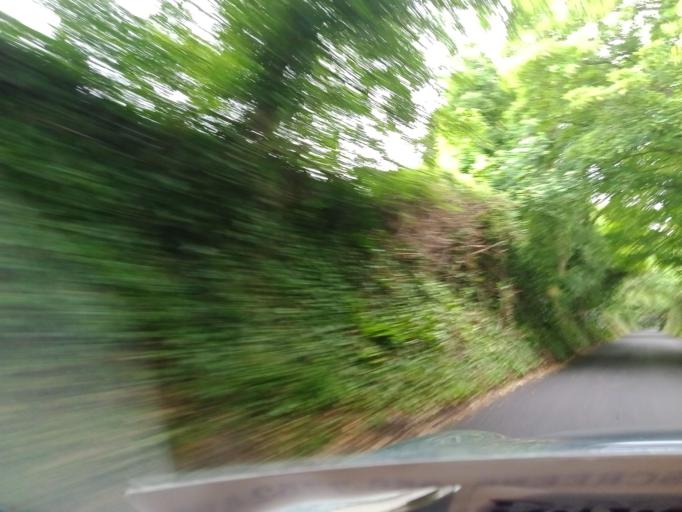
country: IE
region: Leinster
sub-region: Kilkenny
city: Thomastown
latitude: 52.5469
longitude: -7.2245
